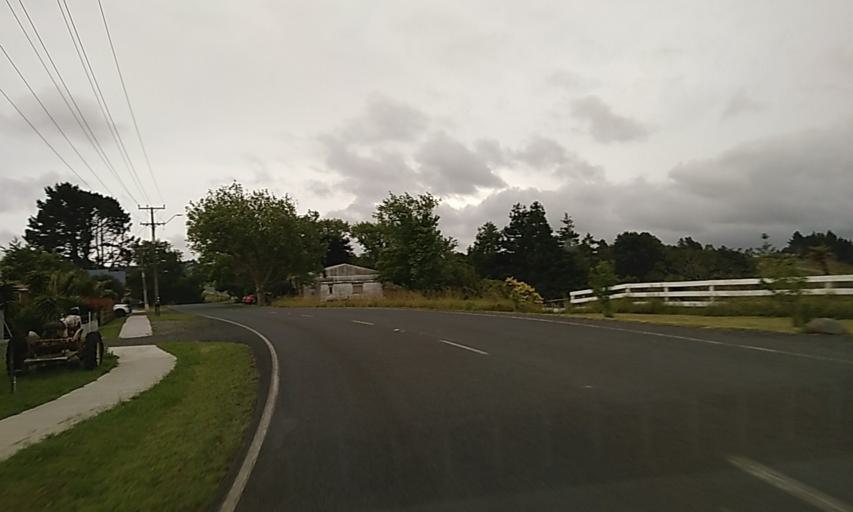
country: NZ
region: Auckland
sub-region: Auckland
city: Pukekohe East
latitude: -37.3261
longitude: 174.9163
